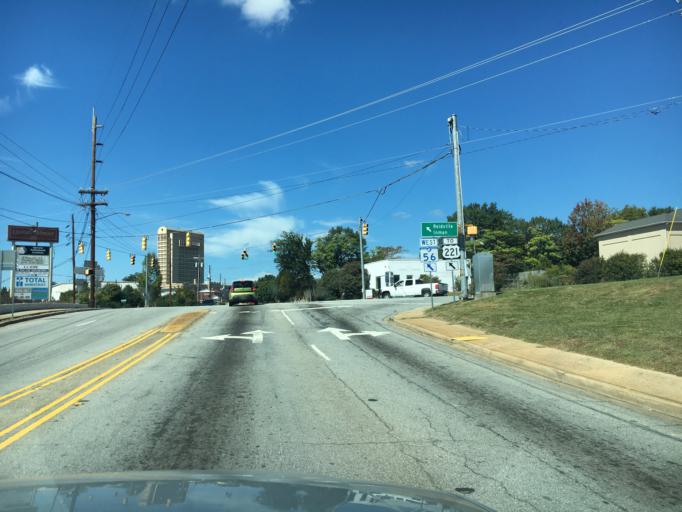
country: US
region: South Carolina
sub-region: Spartanburg County
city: Spartanburg
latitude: 34.9473
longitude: -81.9221
